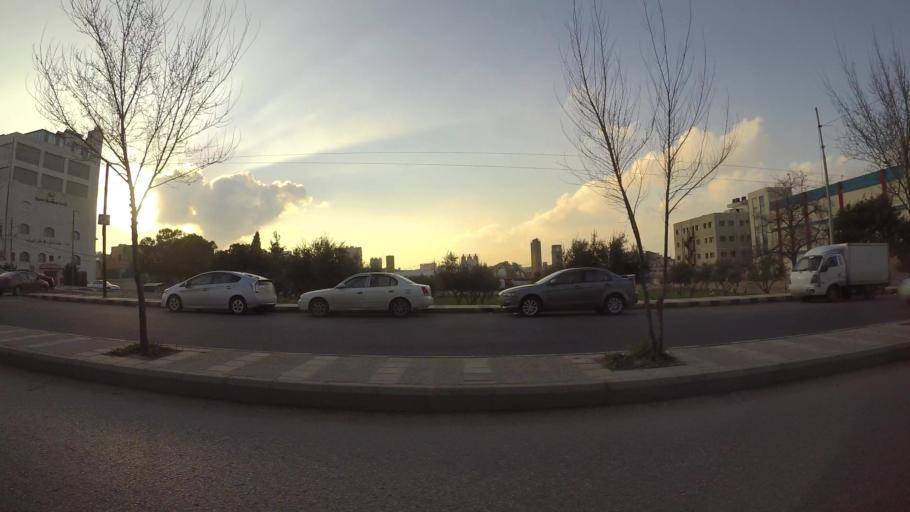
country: JO
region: Amman
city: Al Bunayyat ash Shamaliyah
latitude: 31.9118
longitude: 35.9146
